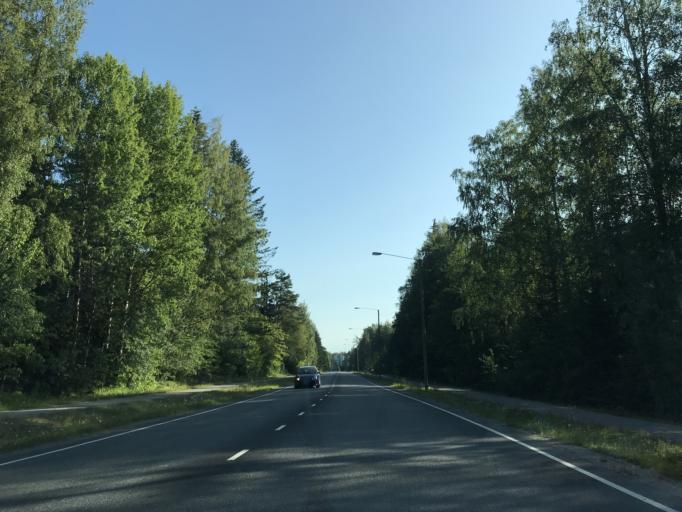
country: FI
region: Paijanne Tavastia
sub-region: Lahti
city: Orimattila
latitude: 60.7970
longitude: 25.7232
